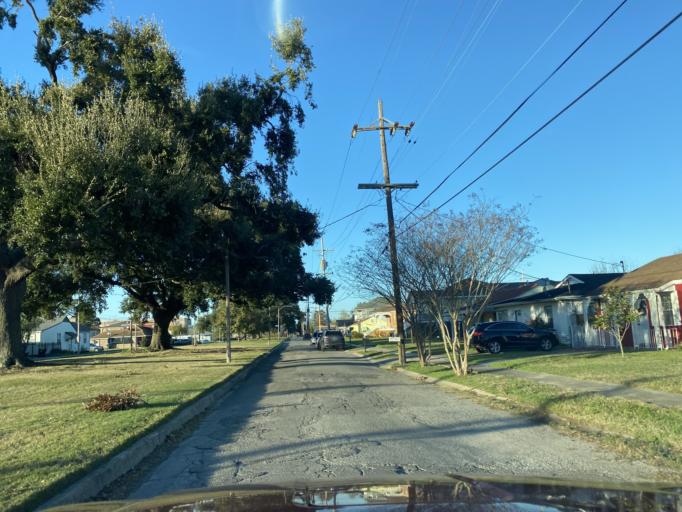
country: US
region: Louisiana
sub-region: Orleans Parish
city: New Orleans
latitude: 30.0149
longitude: -90.0557
